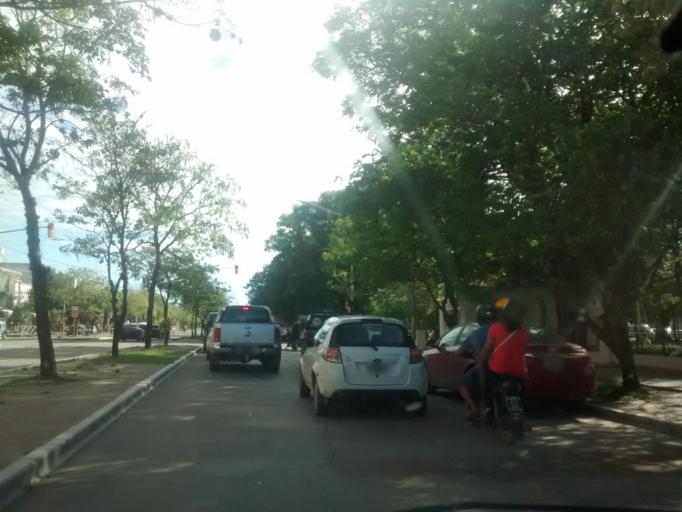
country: AR
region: Chaco
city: Resistencia
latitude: -27.4632
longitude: -58.9858
